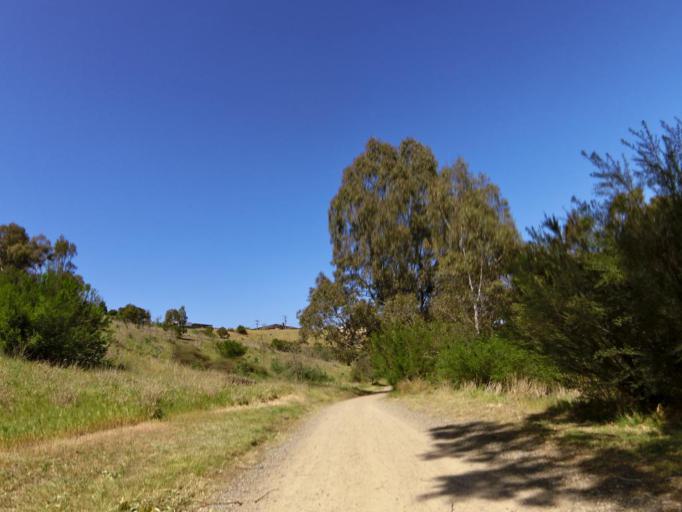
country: AU
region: Victoria
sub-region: Brimbank
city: Albion
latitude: -37.7633
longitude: 144.8542
